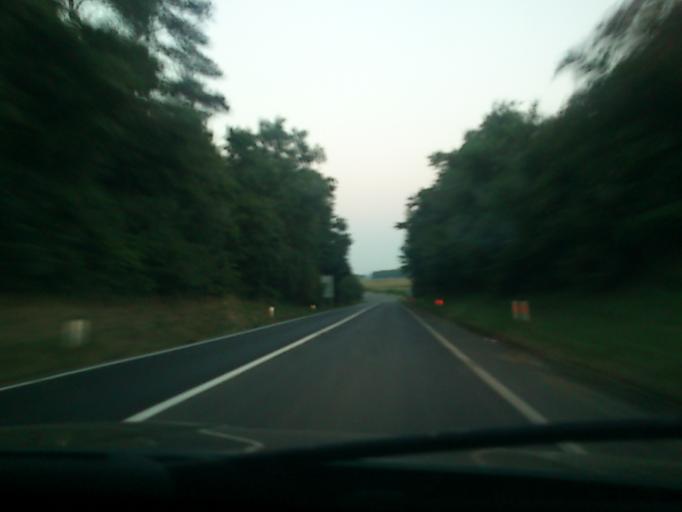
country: SI
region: Duplek
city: Zgornji Duplek
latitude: 46.4943
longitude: 15.7166
